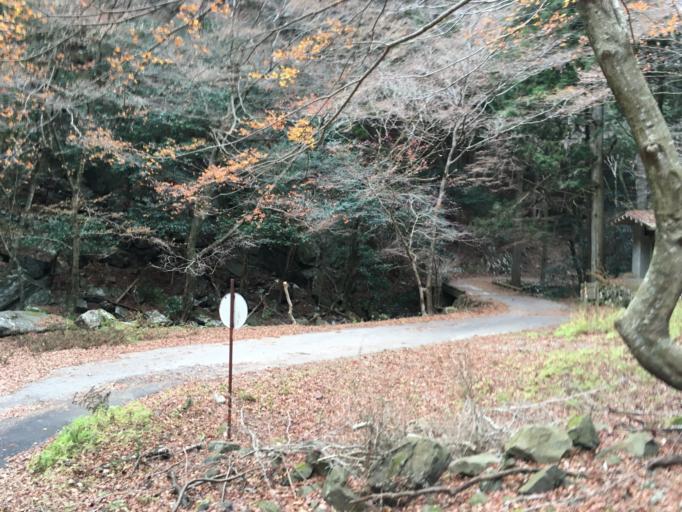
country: JP
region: Aichi
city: Shinshiro
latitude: 34.9171
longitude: 137.4105
